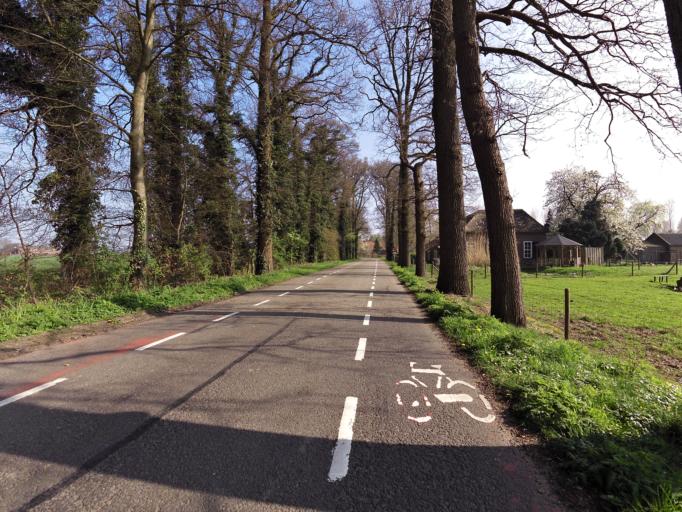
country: NL
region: Gelderland
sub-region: Gemeente Bronckhorst
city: Baak
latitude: 52.0722
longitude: 6.2374
